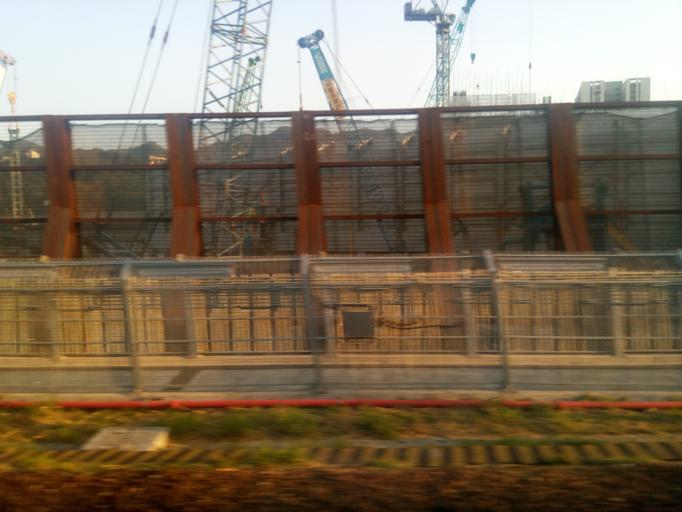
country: HK
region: Sha Tin
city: Sha Tin
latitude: 22.3740
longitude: 114.1797
